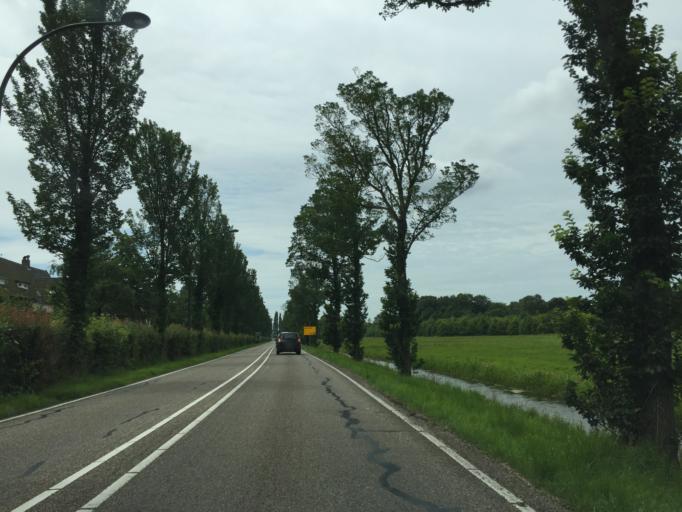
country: NL
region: South Holland
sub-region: Gemeente Leidschendam-Voorburg
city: Voorburg
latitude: 52.1128
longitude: 4.3572
